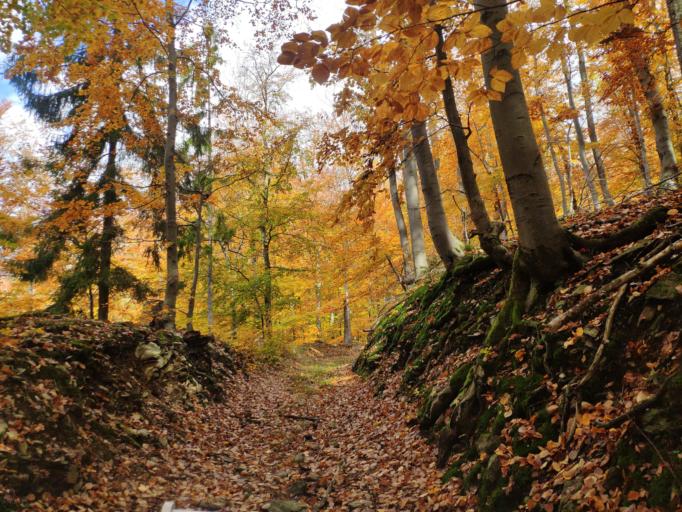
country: SK
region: Kosicky
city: Medzev
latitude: 48.7315
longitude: 20.9871
